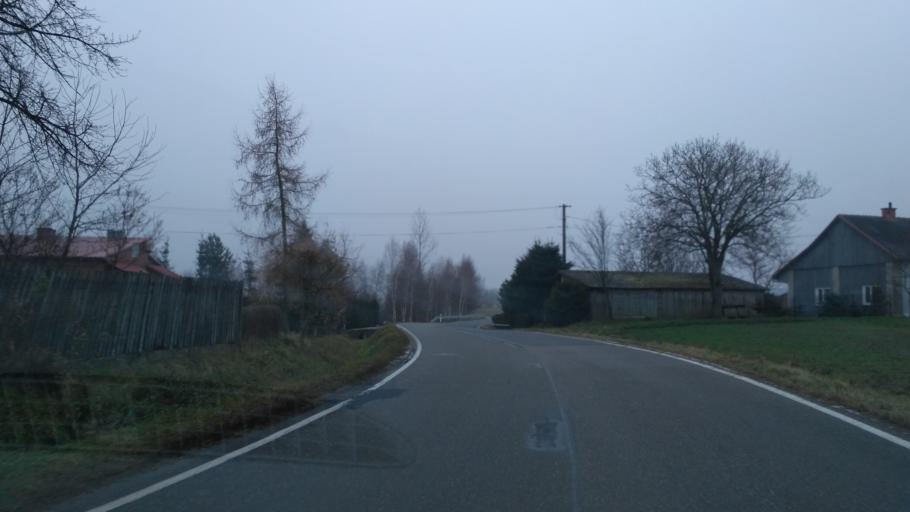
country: PL
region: Subcarpathian Voivodeship
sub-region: Powiat lancucki
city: Handzlowka
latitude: 49.9672
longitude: 22.1911
